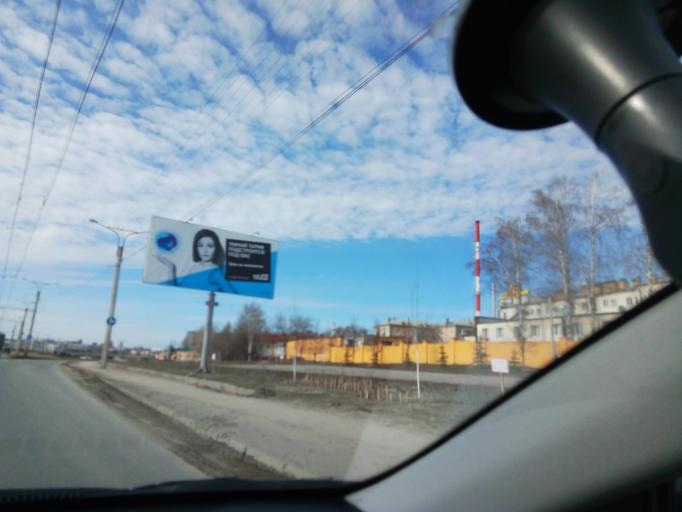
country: RU
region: Chuvashia
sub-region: Cheboksarskiy Rayon
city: Cheboksary
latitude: 56.1203
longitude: 47.2498
